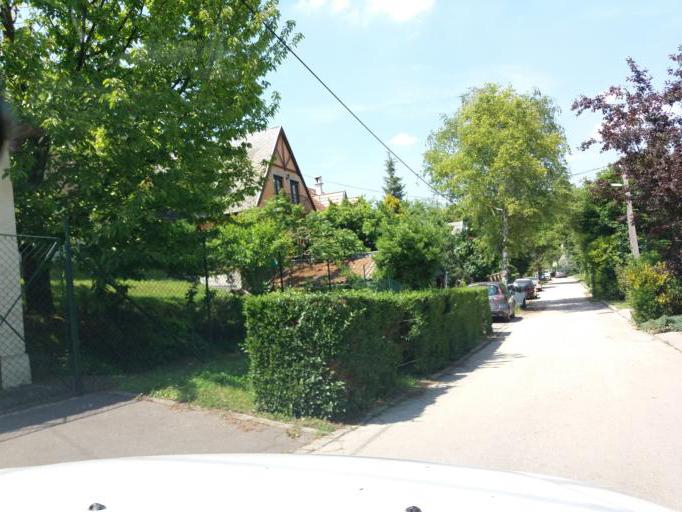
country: HU
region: Budapest
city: Budapest XXII. keruelet
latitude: 47.4434
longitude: 19.0281
